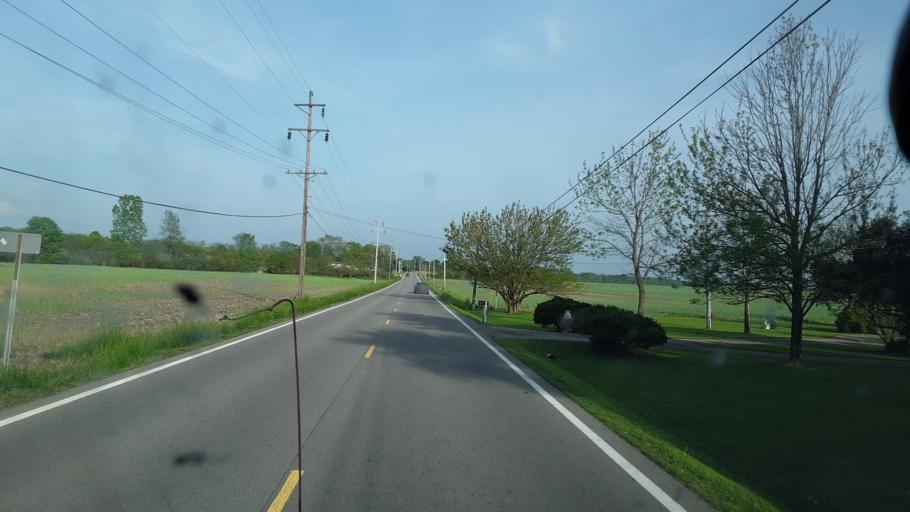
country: US
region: Ohio
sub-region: Pickaway County
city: Logan Elm Village
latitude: 39.5627
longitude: -82.8820
